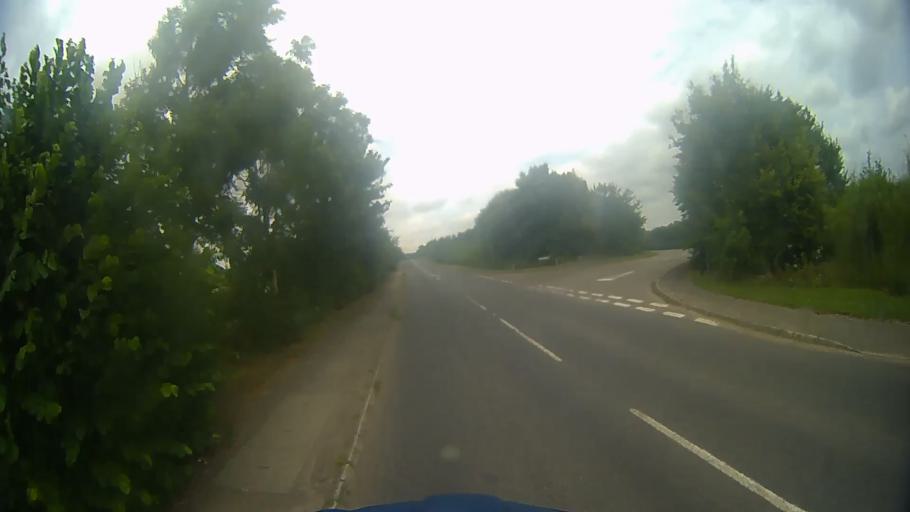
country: GB
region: England
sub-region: Hampshire
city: Kingsley
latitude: 51.1849
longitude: -0.8777
